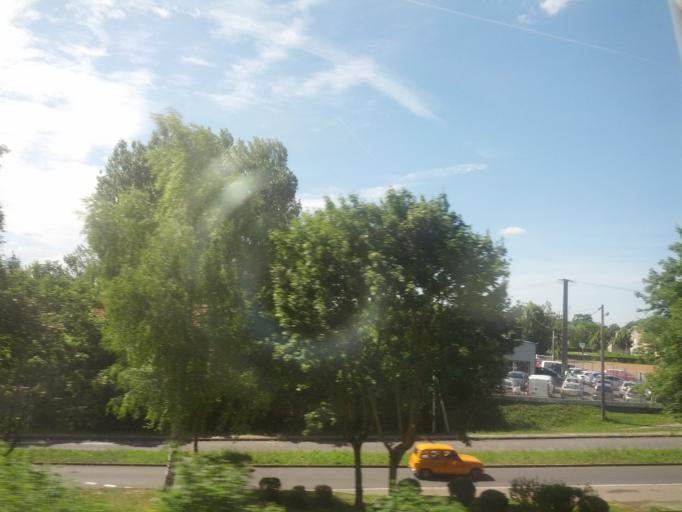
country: FR
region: Poitou-Charentes
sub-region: Departement de la Charente
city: La Couronne
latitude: 45.6279
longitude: 0.1176
